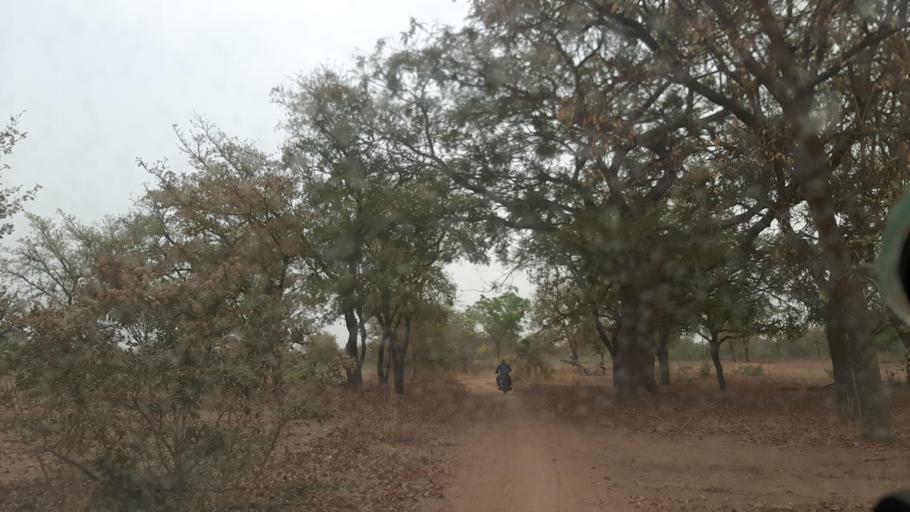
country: BF
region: Boucle du Mouhoun
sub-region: Province des Banwa
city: Salanso
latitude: 11.8556
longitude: -4.4305
